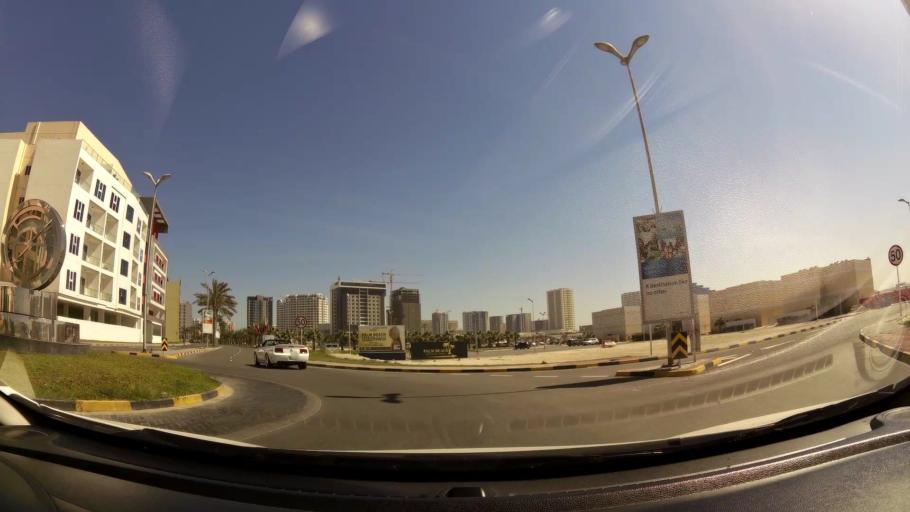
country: BH
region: Muharraq
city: Al Hadd
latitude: 26.2943
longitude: 50.6594
